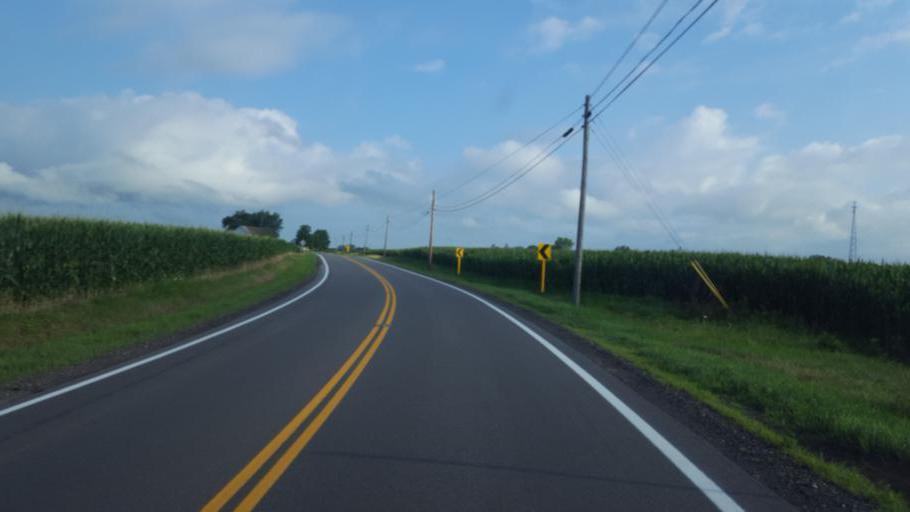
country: US
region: Ohio
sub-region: Richland County
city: Shelby
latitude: 40.8385
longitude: -82.6569
